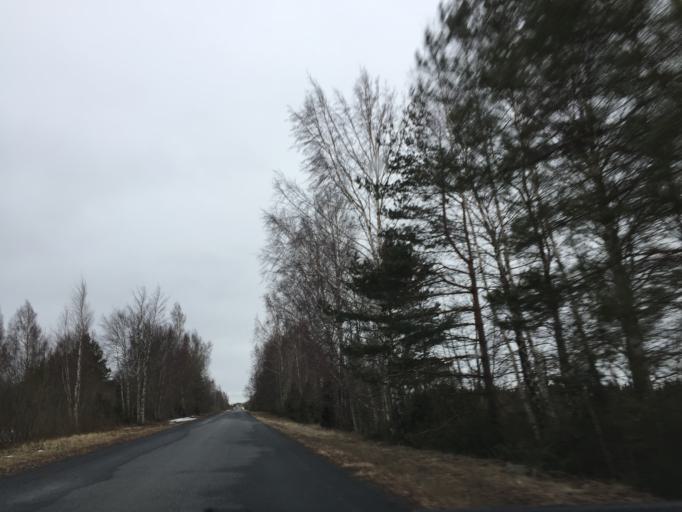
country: EE
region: Laeaene
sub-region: Haapsalu linn
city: Haapsalu
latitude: 58.7755
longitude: 23.4606
